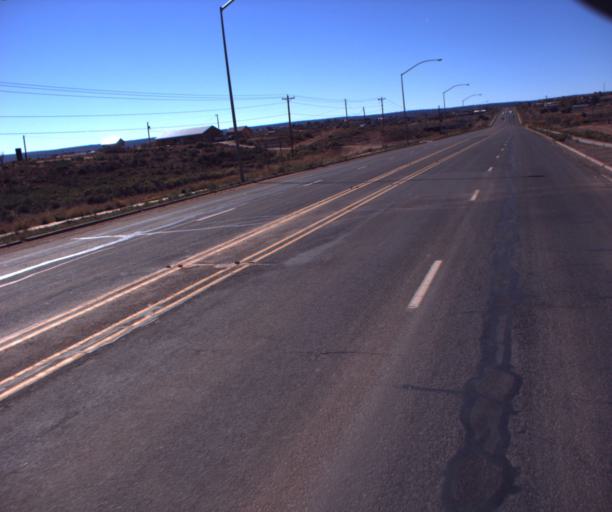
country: US
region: Arizona
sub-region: Apache County
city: Saint Michaels
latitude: 35.6592
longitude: -109.0798
